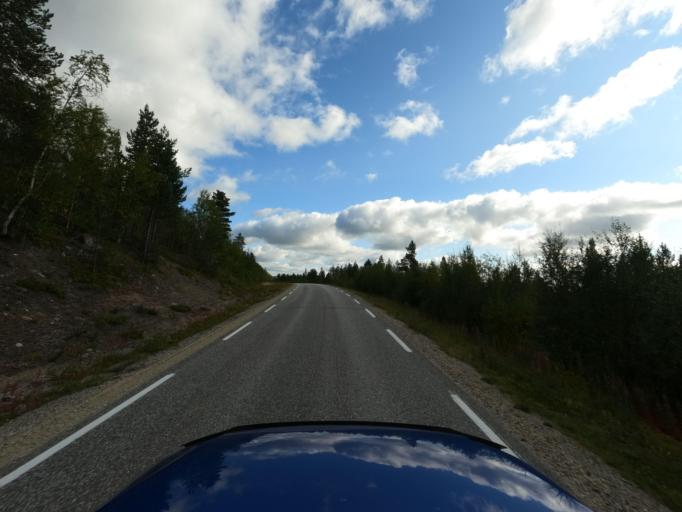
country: NO
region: Finnmark Fylke
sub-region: Karasjok
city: Karasjohka
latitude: 69.4424
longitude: 25.2567
